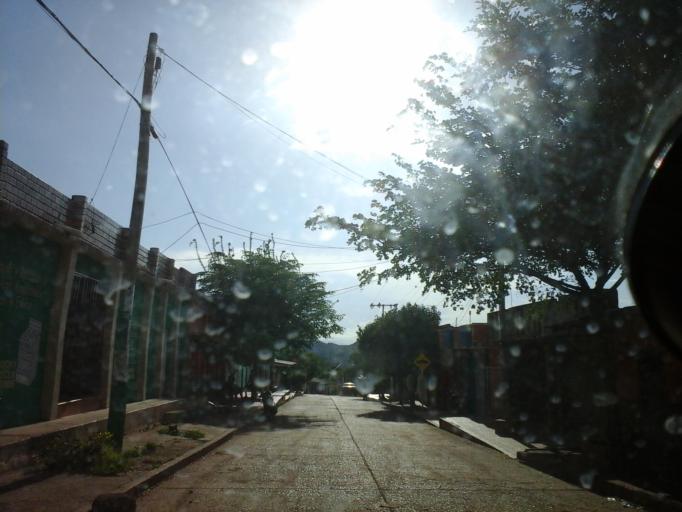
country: CO
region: Cesar
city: San Diego
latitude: 10.2427
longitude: -73.1384
